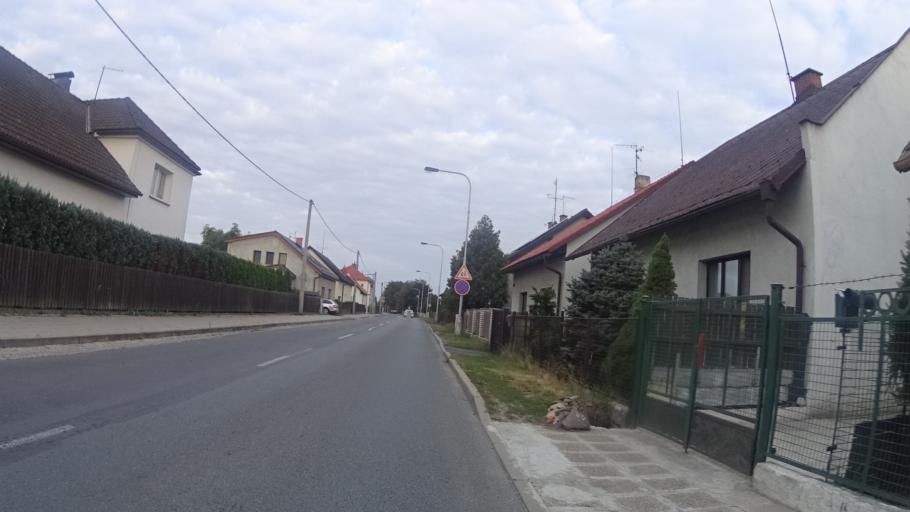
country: CZ
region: Kralovehradecky
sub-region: Okres Hradec Kralove
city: Hradec Kralove
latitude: 50.2068
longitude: 15.8760
